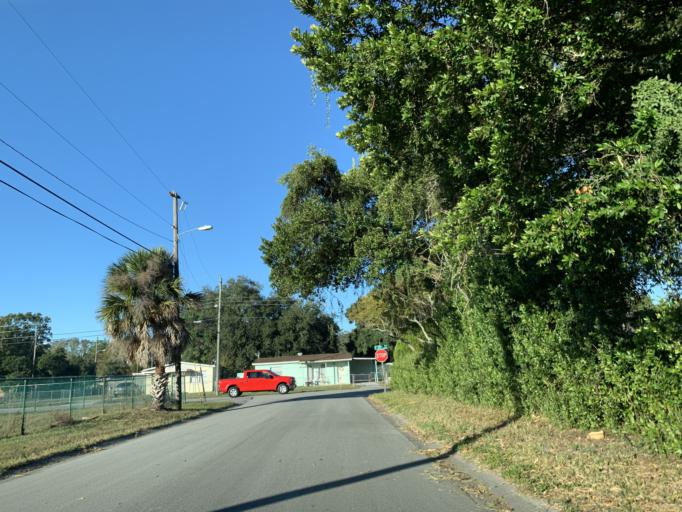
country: US
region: Florida
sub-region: Hillsborough County
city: University
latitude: 28.0420
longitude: -82.4289
